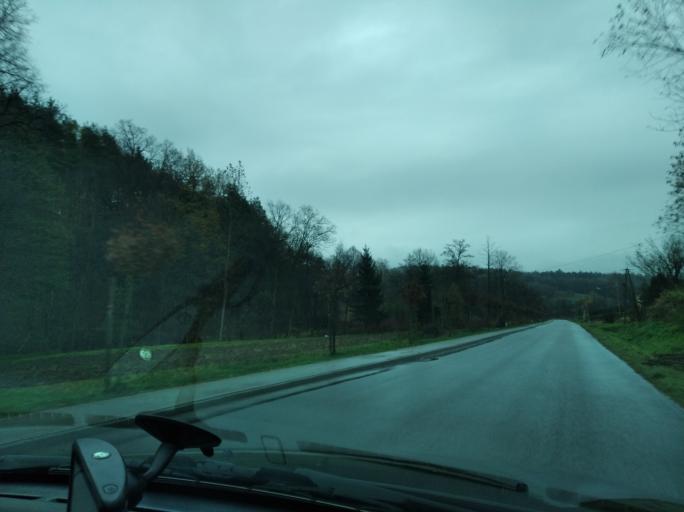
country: PL
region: Subcarpathian Voivodeship
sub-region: Powiat rzeszowski
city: Straszydle
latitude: 49.9011
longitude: 22.0043
